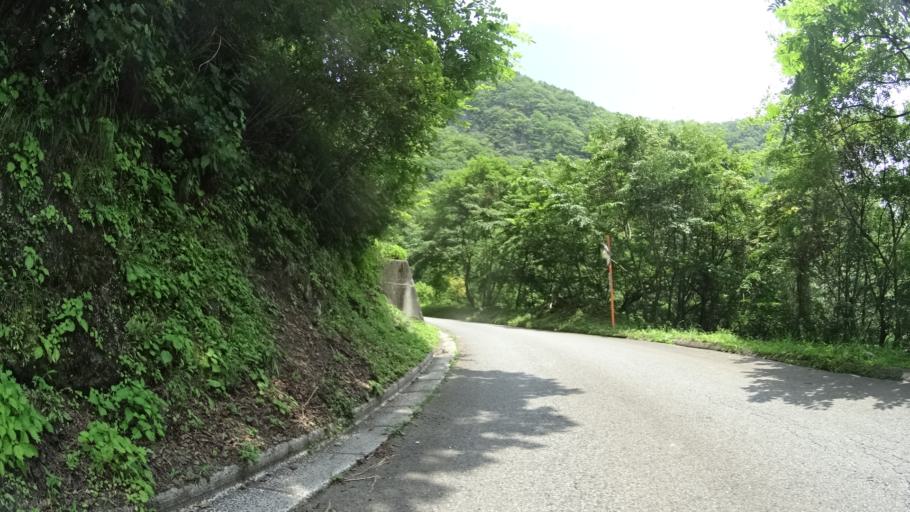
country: JP
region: Nagano
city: Saku
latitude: 36.0930
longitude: 138.6842
